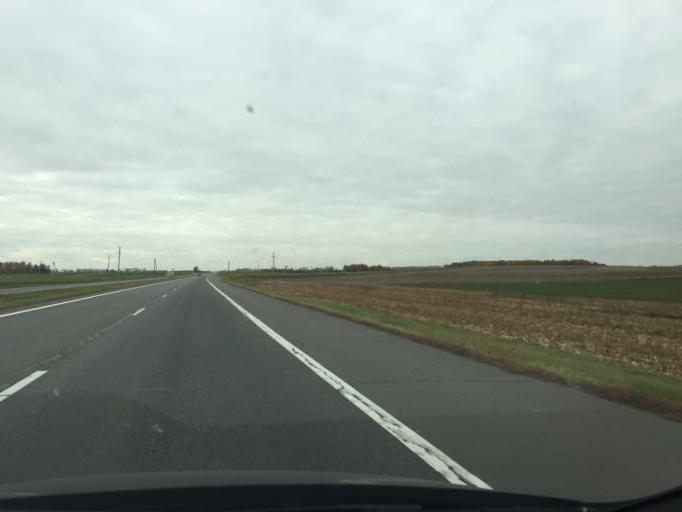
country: BY
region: Minsk
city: Atolina
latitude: 53.6981
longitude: 27.4122
